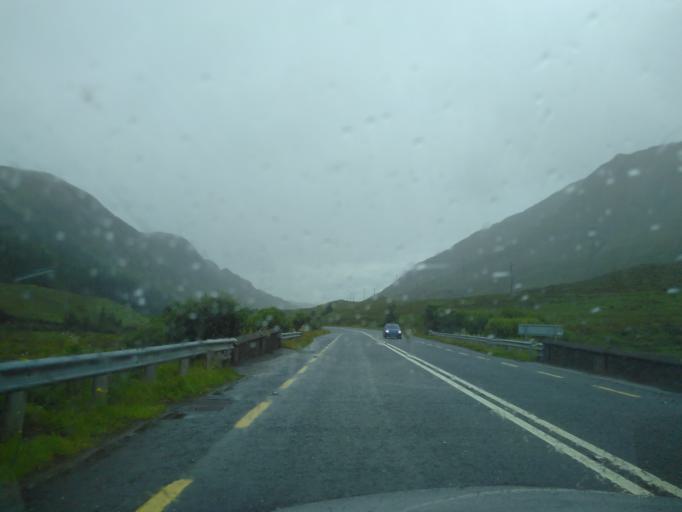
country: IE
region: Ulster
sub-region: County Donegal
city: Ballybofey
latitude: 54.7314
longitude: -7.9388
